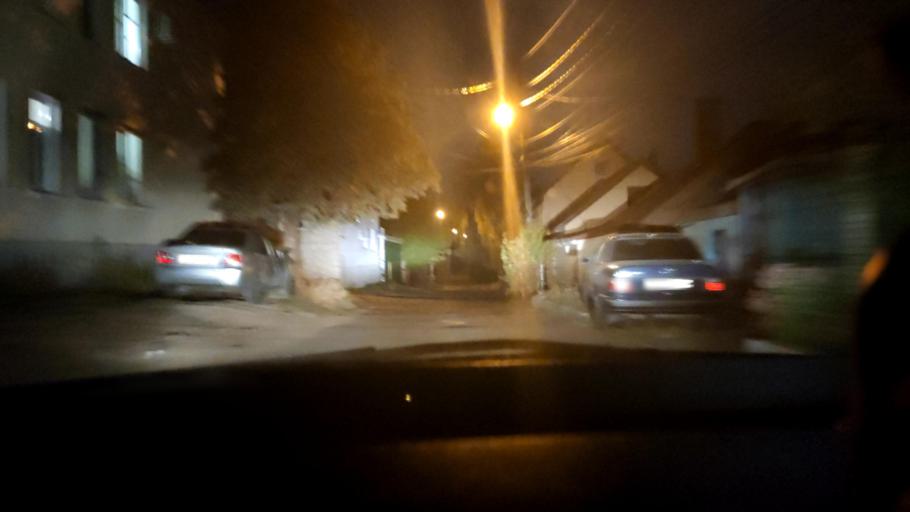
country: RU
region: Voronezj
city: Voronezh
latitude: 51.6807
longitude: 39.2207
